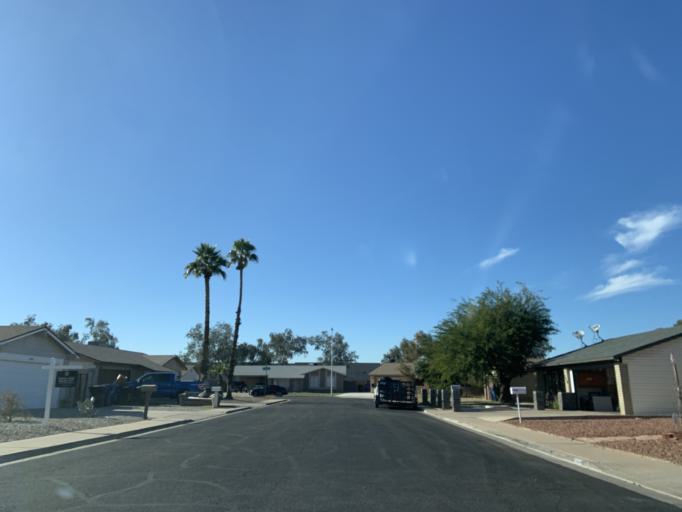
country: US
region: Arizona
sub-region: Maricopa County
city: San Carlos
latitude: 33.3623
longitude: -111.8743
